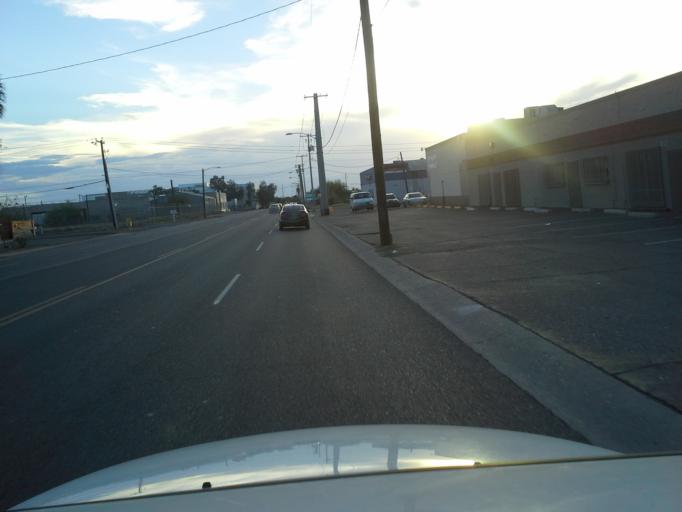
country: US
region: Arizona
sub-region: Maricopa County
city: Phoenix
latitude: 33.4369
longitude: -112.0664
